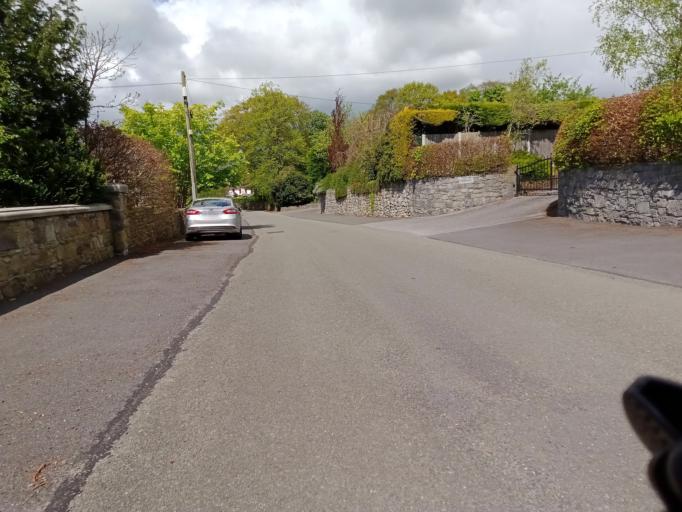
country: IE
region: Leinster
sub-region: Kilkenny
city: Kilkenny
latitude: 52.6693
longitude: -7.2583
